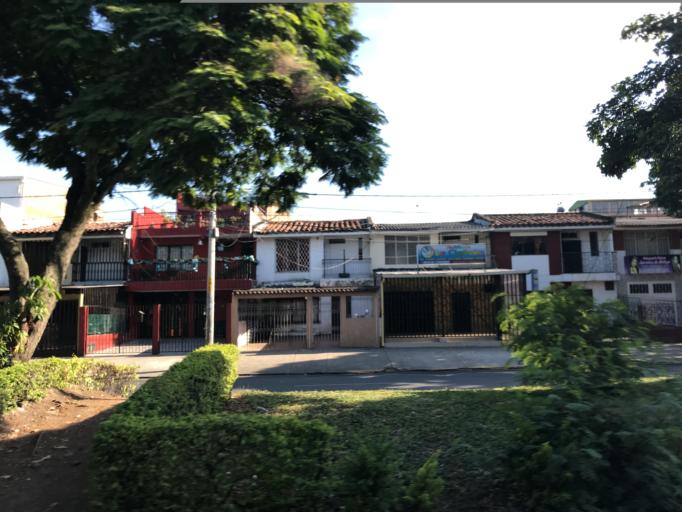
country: CO
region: Valle del Cauca
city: Cali
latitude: 3.4695
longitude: -76.4976
